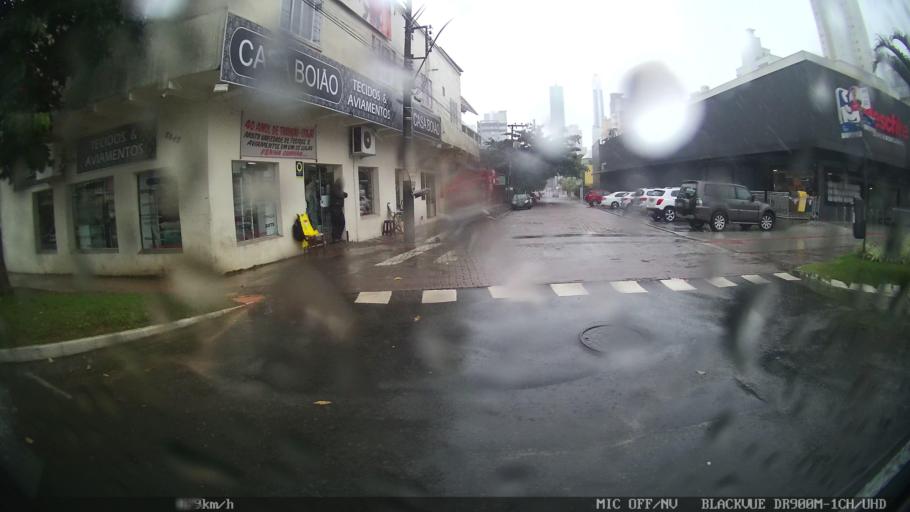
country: BR
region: Santa Catarina
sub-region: Balneario Camboriu
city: Balneario Camboriu
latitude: -26.9822
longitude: -48.6400
